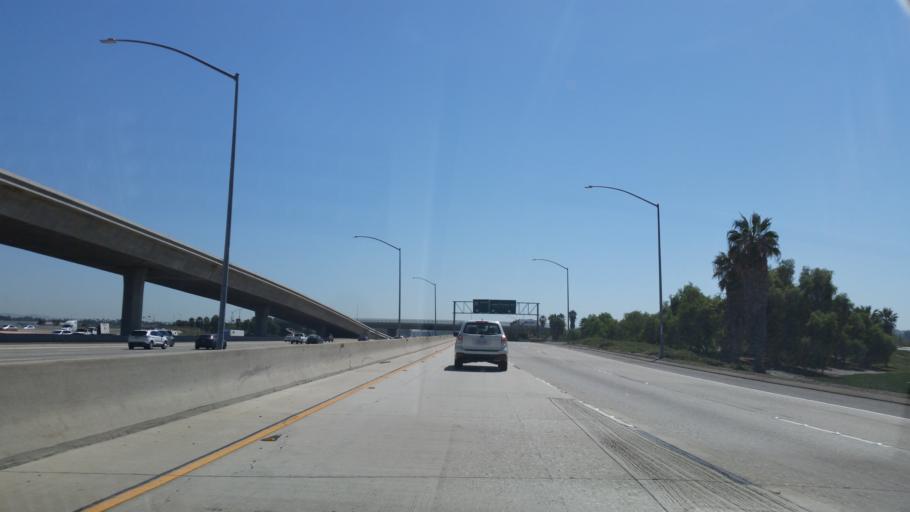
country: US
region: California
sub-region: Orange County
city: Laguna Woods
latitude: 33.6421
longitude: -117.7334
